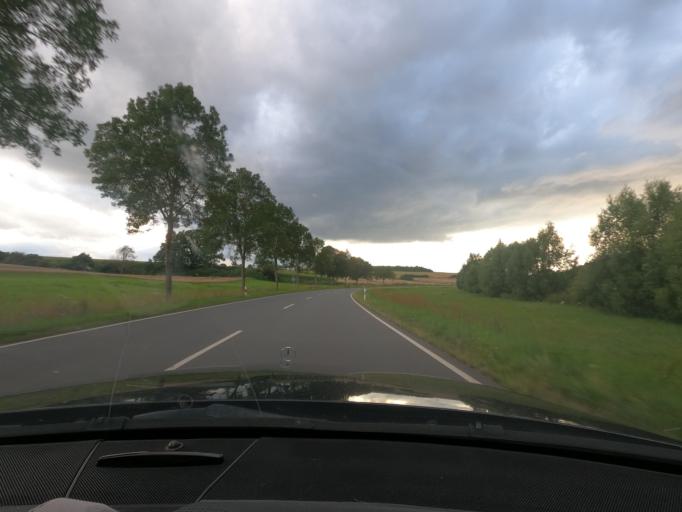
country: DE
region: Hesse
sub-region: Regierungsbezirk Kassel
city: Wolfhagen
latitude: 51.3126
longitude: 9.1964
